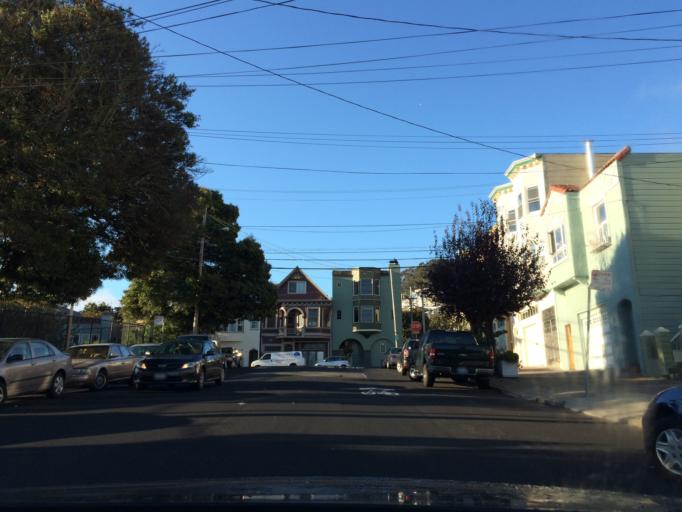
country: US
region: California
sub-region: San Francisco County
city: San Francisco
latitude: 37.7425
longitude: -122.4288
